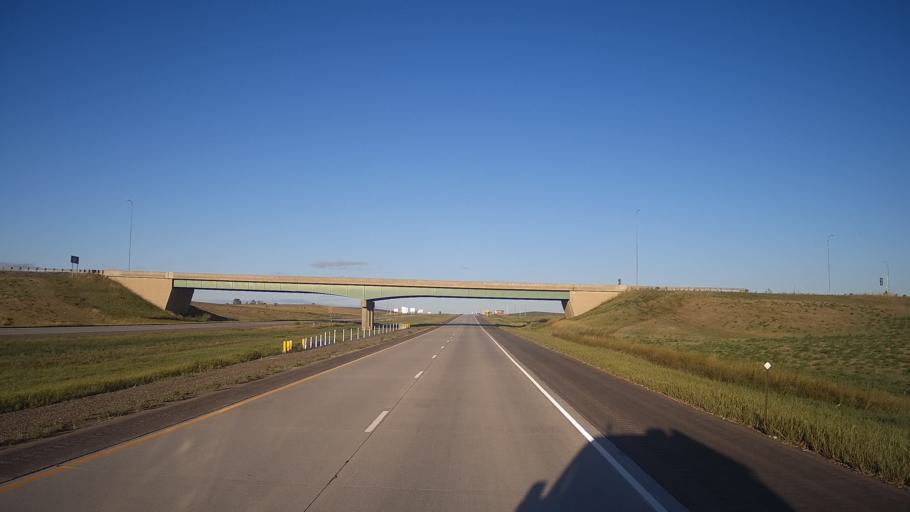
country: US
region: South Dakota
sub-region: Jones County
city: Murdo
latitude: 43.8830
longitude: -100.7076
